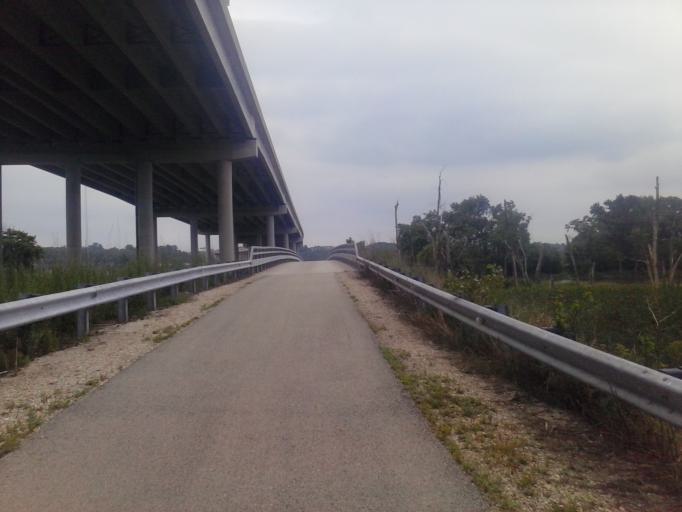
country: US
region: Illinois
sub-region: Cook County
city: Lemont
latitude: 41.6739
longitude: -88.0299
